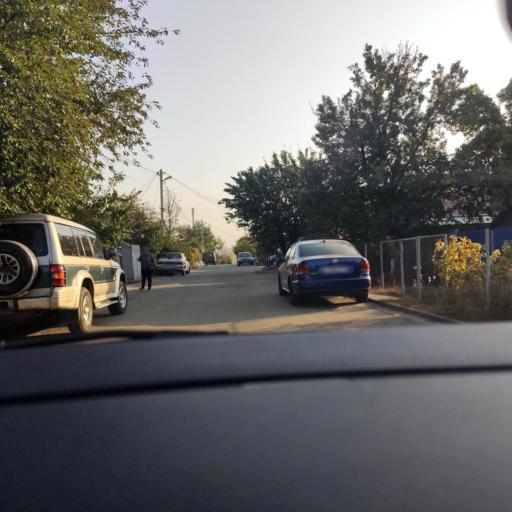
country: RU
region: Voronezj
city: Podgornoye
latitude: 51.6992
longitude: 39.1531
